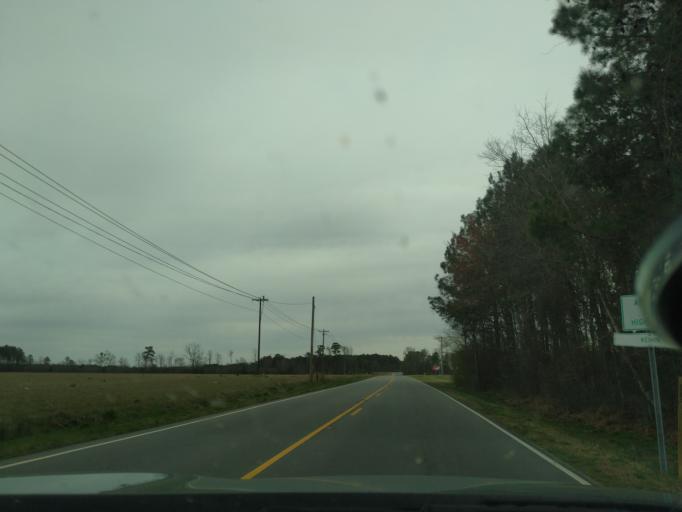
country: US
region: North Carolina
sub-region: Edgecombe County
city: Tarboro
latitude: 35.8931
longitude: -77.5915
